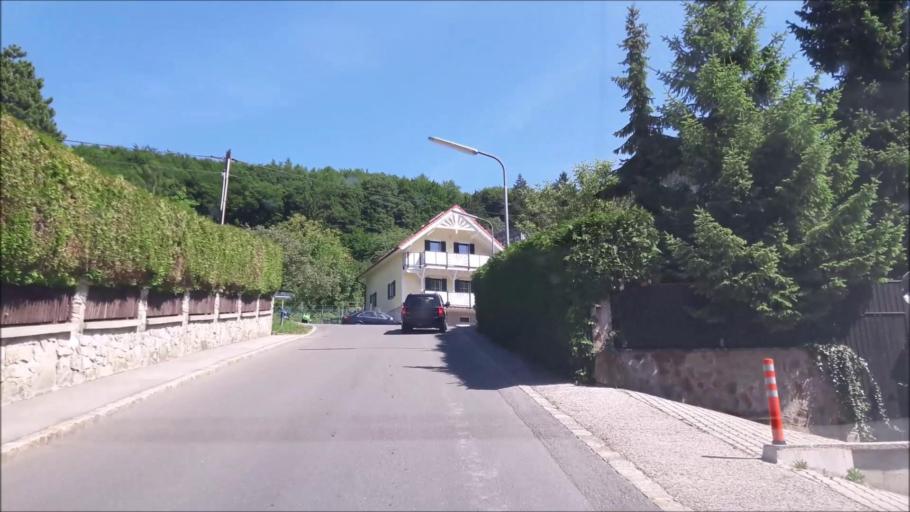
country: AT
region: Lower Austria
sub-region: Politischer Bezirk Wien-Umgebung
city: Mauerbach
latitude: 48.2464
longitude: 16.2170
